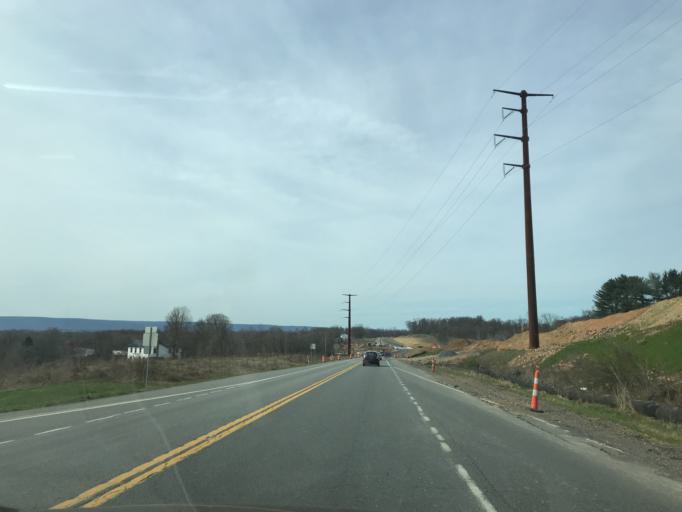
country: US
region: Pennsylvania
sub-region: Union County
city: Lewisburg
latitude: 40.9367
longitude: -76.8504
